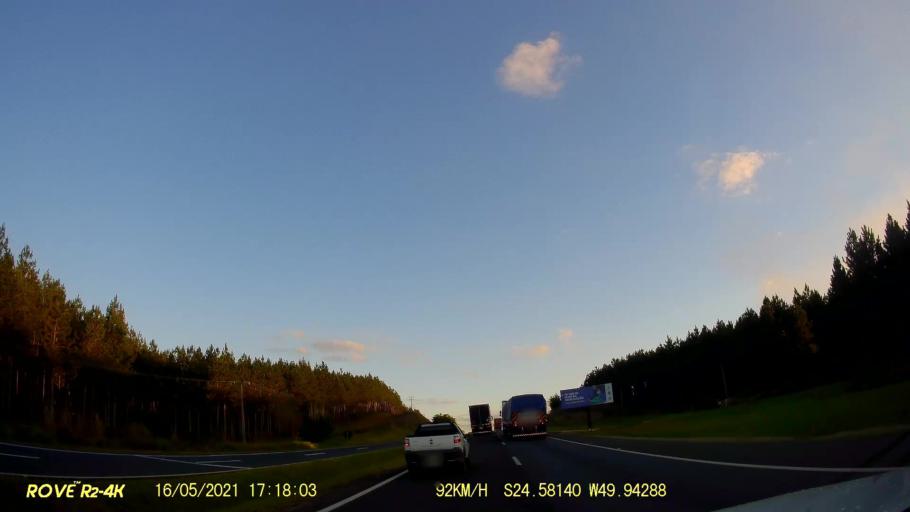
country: BR
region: Parana
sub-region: Pirai Do Sul
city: Pirai do Sul
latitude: -24.5816
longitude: -49.9429
